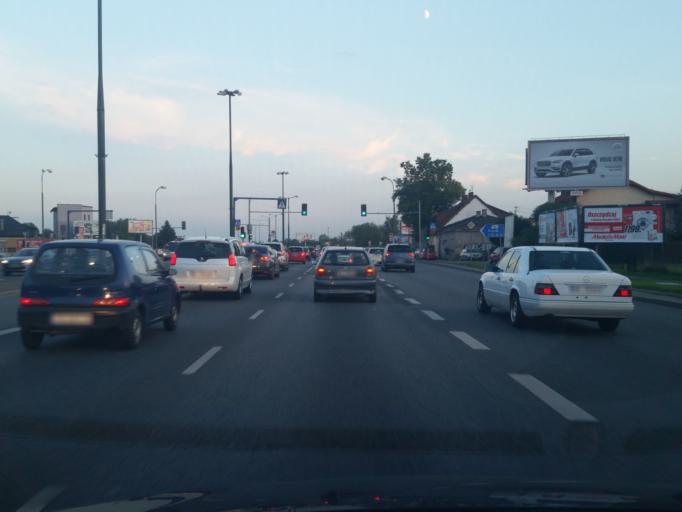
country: PL
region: Masovian Voivodeship
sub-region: Warszawa
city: Bialoleka
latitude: 52.3445
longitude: 20.9506
